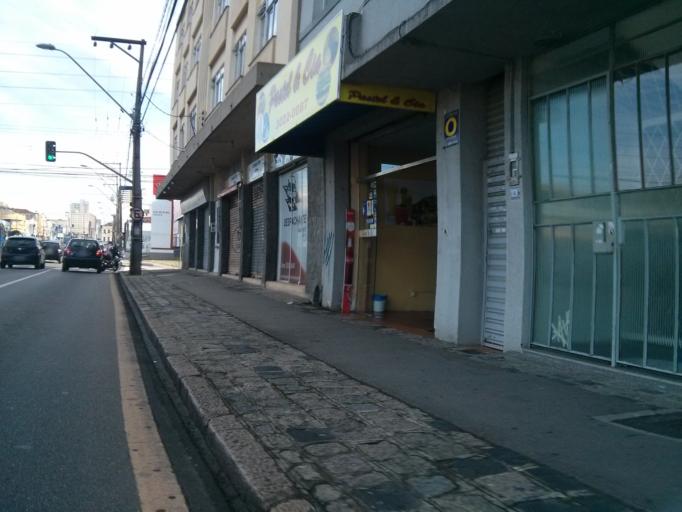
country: BR
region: Parana
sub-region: Curitiba
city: Curitiba
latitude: -25.4458
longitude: -49.2646
